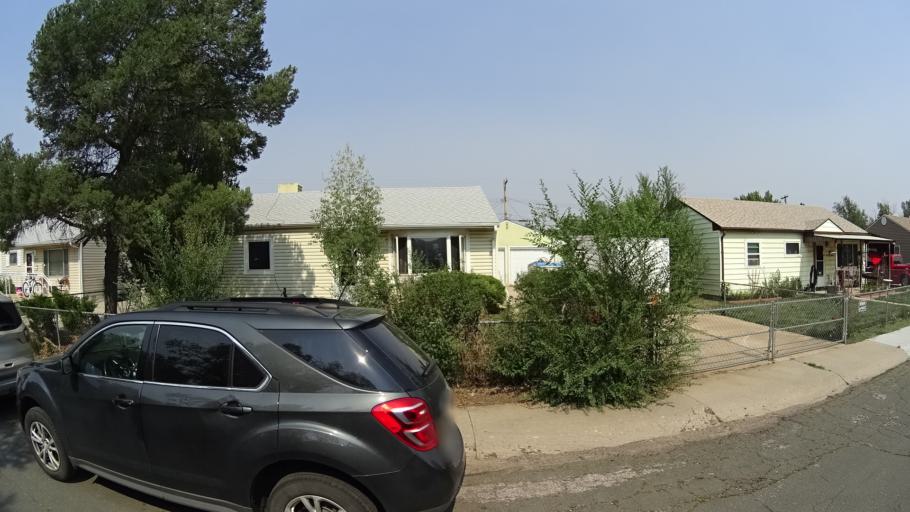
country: US
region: Colorado
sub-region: El Paso County
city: Colorado Springs
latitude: 38.8022
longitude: -104.8055
